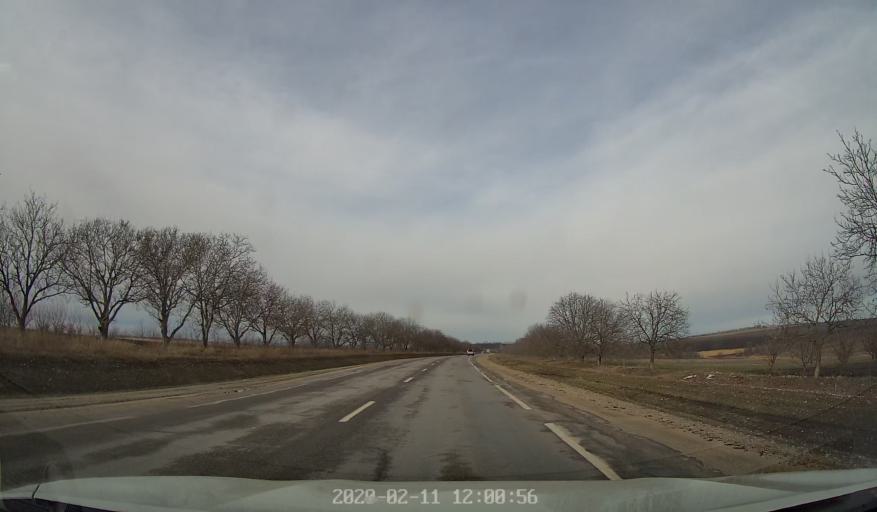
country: MD
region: Riscani
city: Riscani
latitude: 47.9331
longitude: 27.6350
